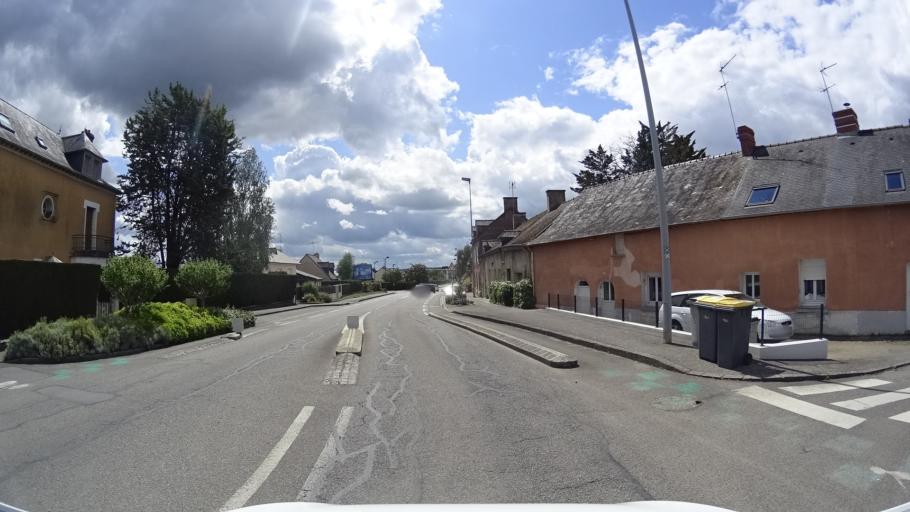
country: FR
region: Brittany
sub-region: Departement d'Ille-et-Vilaine
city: Chartres-de-Bretagne
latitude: 48.0319
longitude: -1.7106
